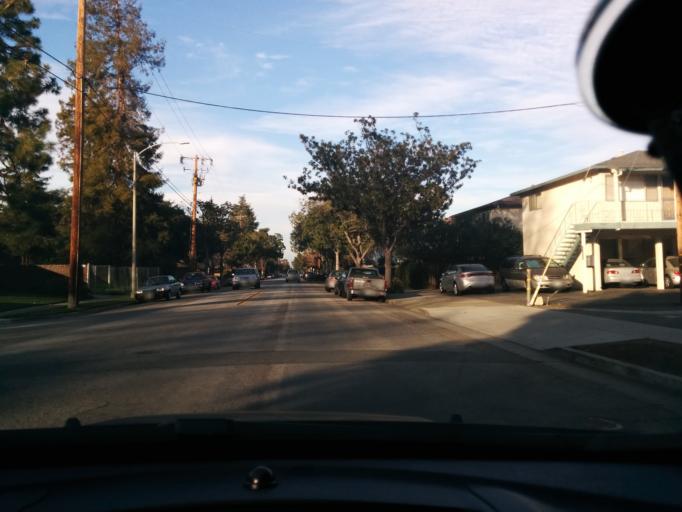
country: US
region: California
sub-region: Santa Clara County
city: Sunnyvale
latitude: 37.3757
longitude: -122.0557
